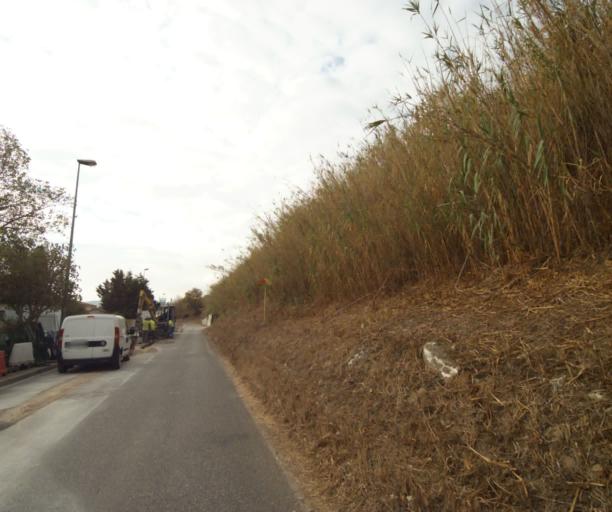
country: FR
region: Provence-Alpes-Cote d'Azur
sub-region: Departement des Bouches-du-Rhone
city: Saint-Victoret
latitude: 43.4142
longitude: 5.2523
